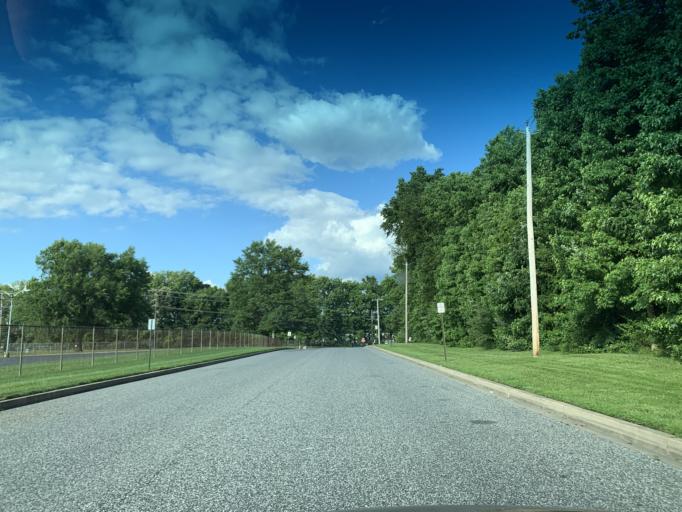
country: US
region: Maryland
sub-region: Harford County
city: Havre de Grace
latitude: 39.5332
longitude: -76.1093
